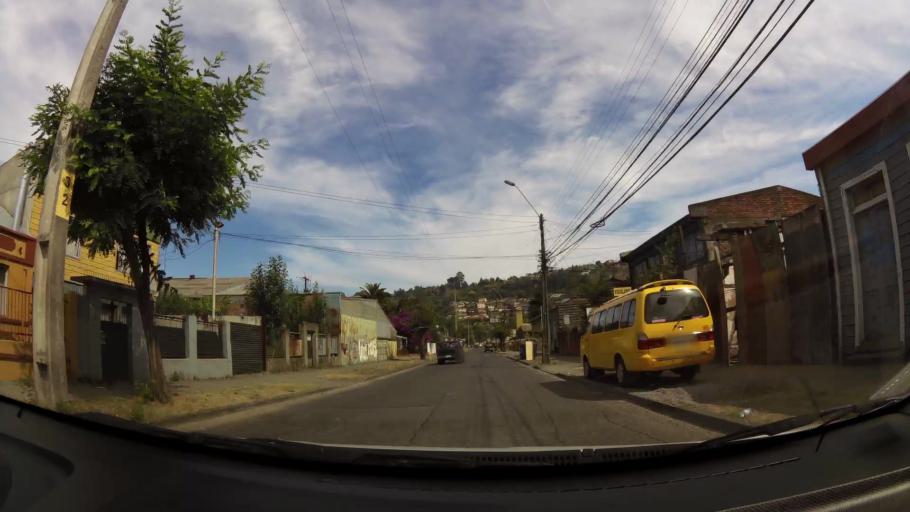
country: CL
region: Biobio
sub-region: Provincia de Concepcion
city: Talcahuano
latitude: -36.7227
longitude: -73.1225
